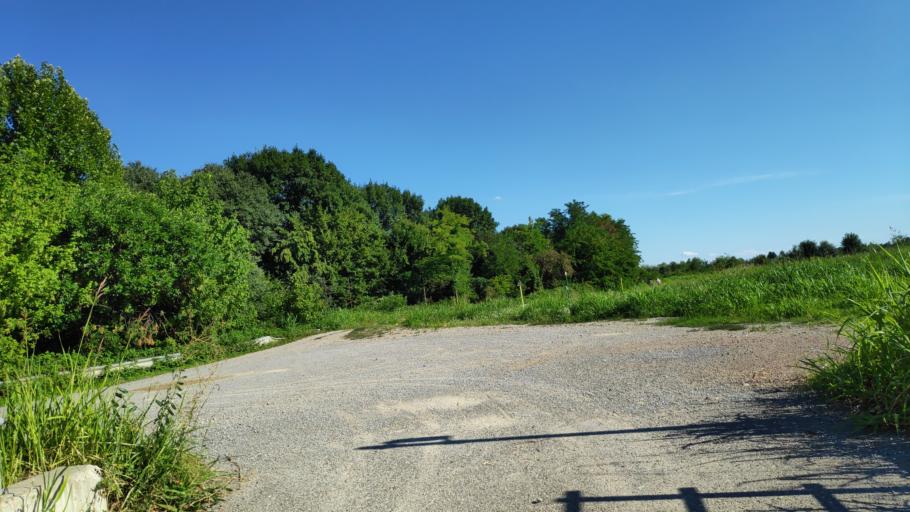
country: IT
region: Lombardy
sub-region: Citta metropolitana di Milano
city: Pozzuolo Martesana
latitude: 45.5057
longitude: 9.4519
